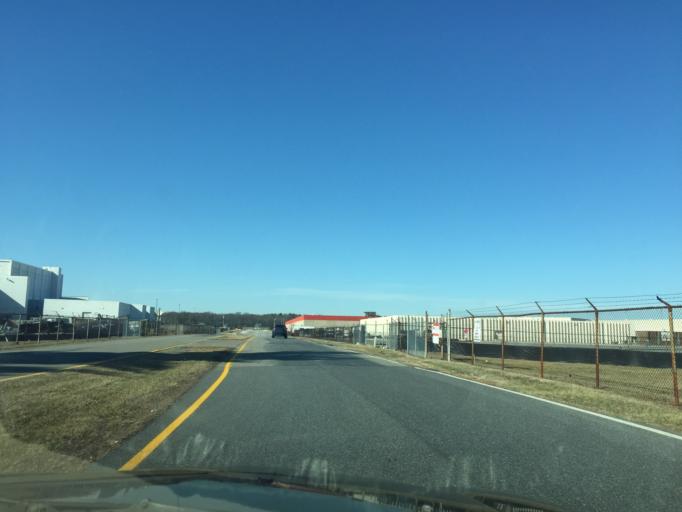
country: US
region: Maryland
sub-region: Baltimore County
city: Middle River
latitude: 39.3275
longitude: -76.4272
